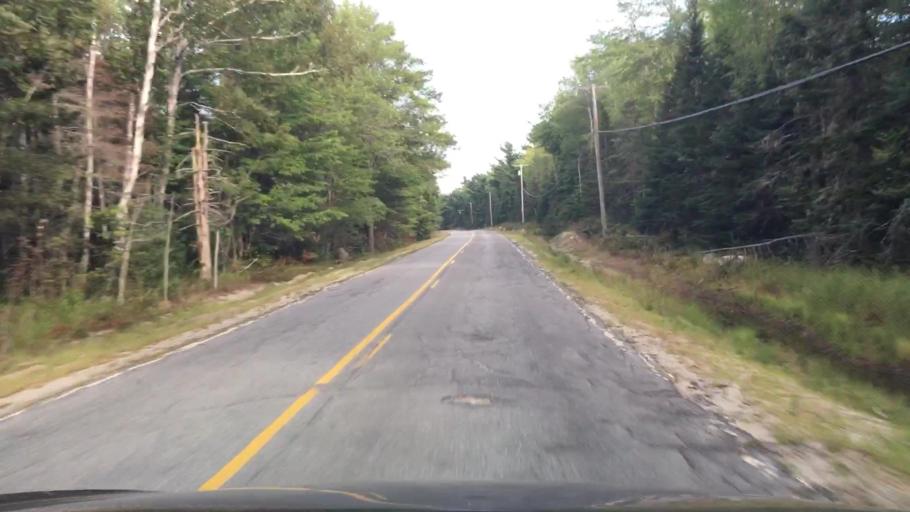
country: US
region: Maine
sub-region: Hancock County
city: Surry
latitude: 44.4989
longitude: -68.5470
